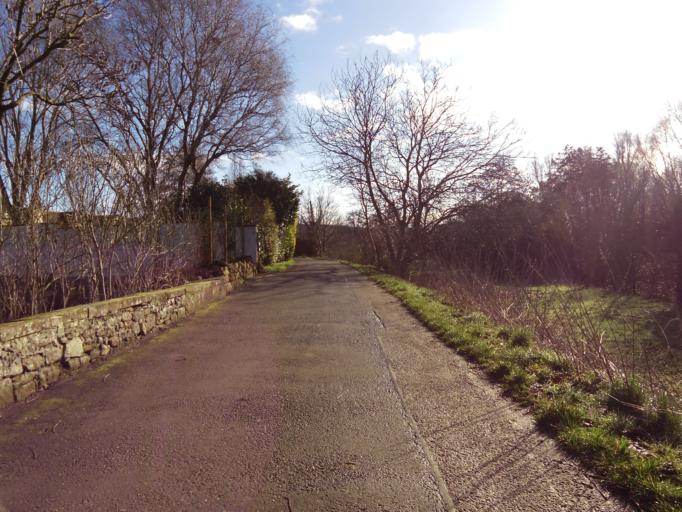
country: DE
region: Rheinland-Pfalz
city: Kirchheim an der Weinstrasse
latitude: 49.5412
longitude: 8.1913
